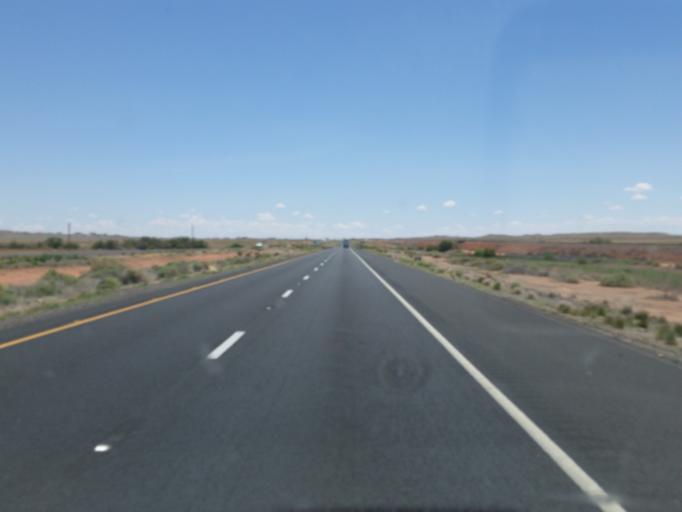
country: US
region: Arizona
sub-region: Coconino County
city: LeChee
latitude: 35.0509
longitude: -110.7796
